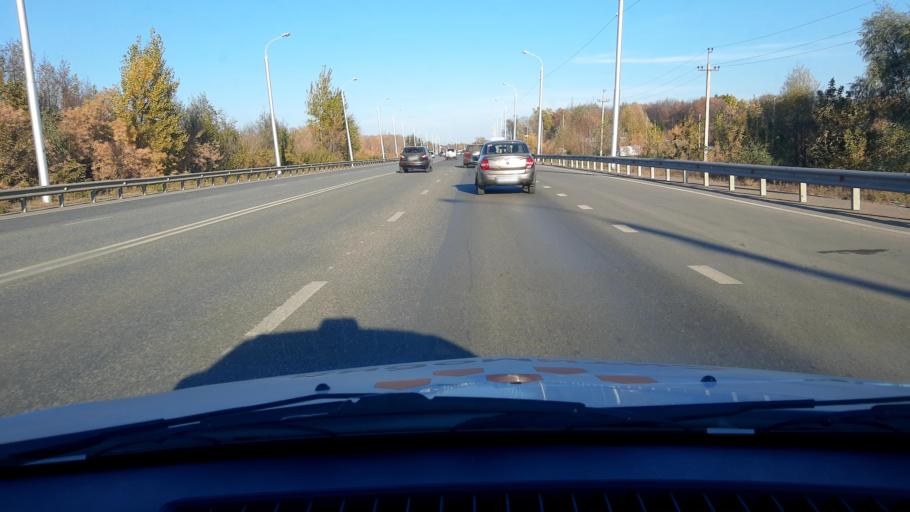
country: RU
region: Bashkortostan
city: Ufa
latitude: 54.8066
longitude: 56.1563
